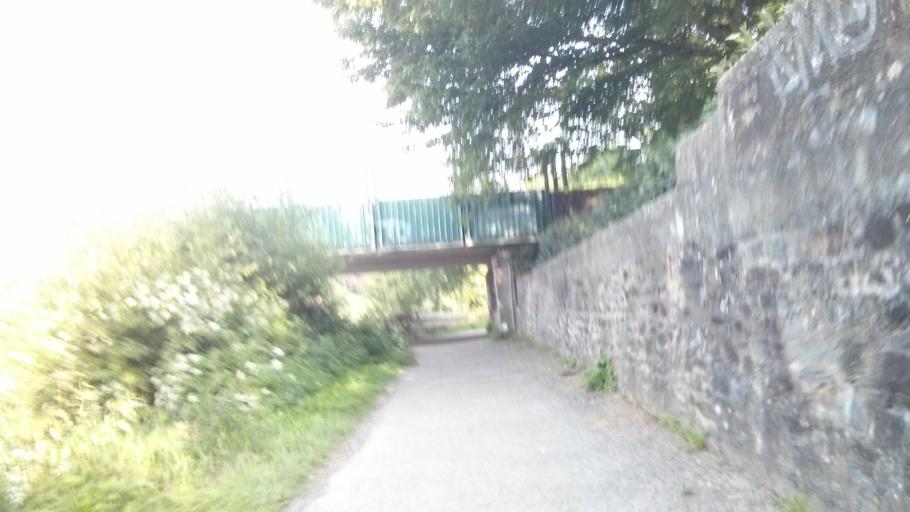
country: FR
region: Pays de la Loire
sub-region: Departement de la Loire-Atlantique
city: Reze
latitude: 47.1832
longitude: -1.5305
